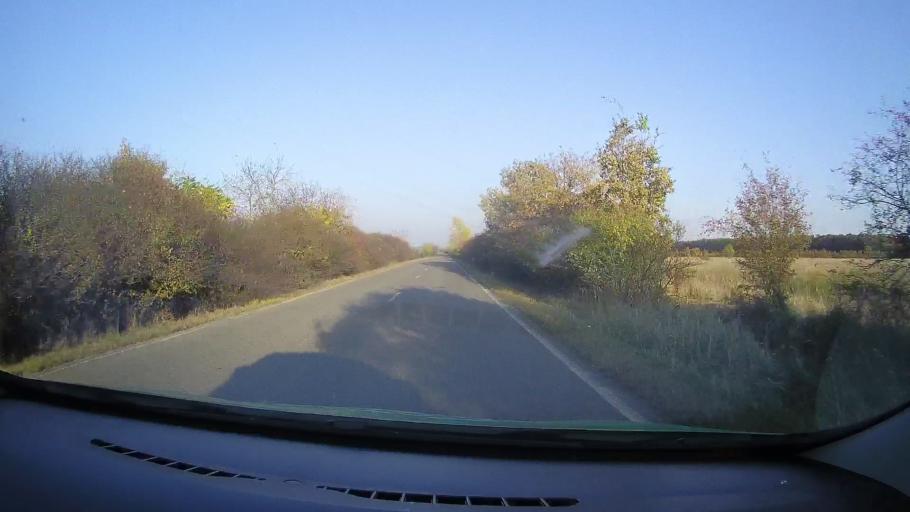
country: RO
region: Arad
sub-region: Comuna Tarnova
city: Chier
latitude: 46.3301
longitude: 21.8478
